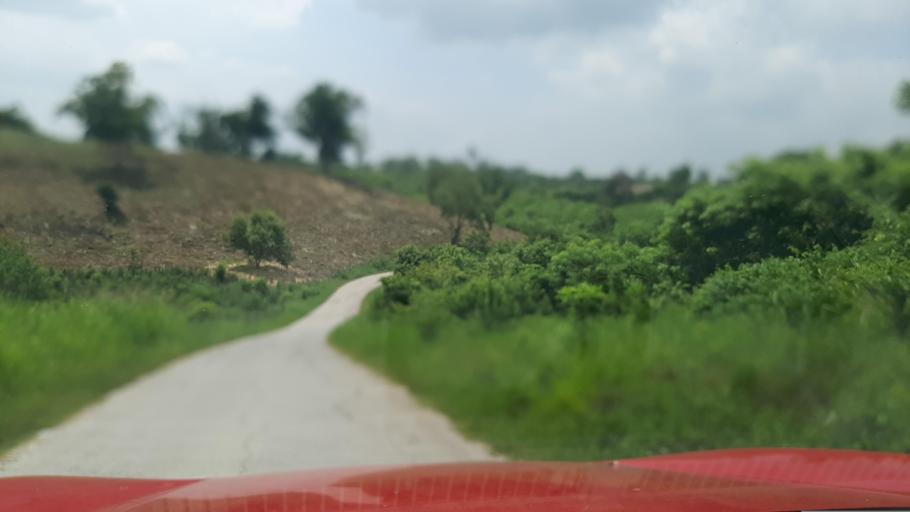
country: MX
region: Veracruz
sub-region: Papantla
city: Polutla
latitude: 20.4543
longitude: -97.2405
